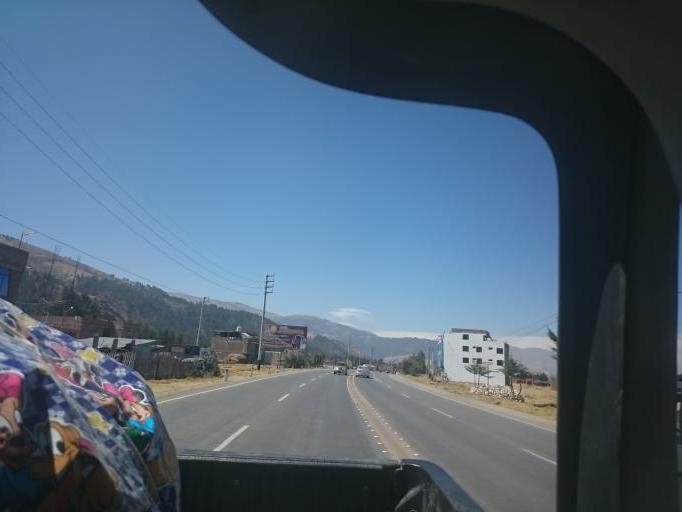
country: PE
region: Junin
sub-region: Provincia de Huancayo
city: San Jeronimo
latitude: -11.9404
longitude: -75.3019
